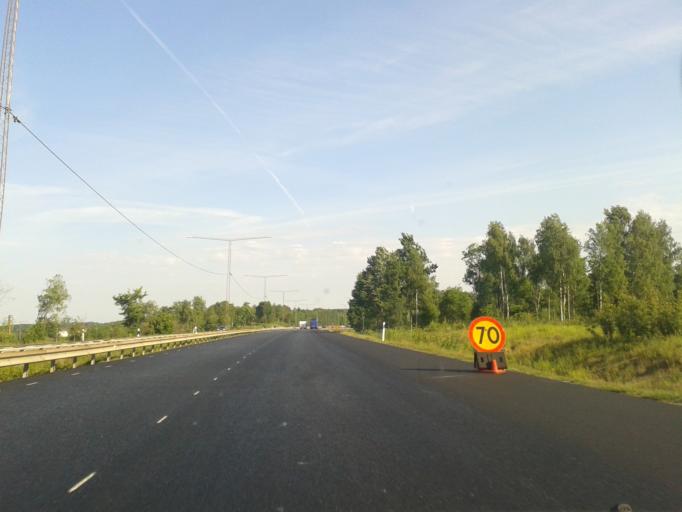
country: SE
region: Vaestra Goetaland
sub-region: Kungalvs Kommun
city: Kode
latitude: 57.9431
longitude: 11.8590
